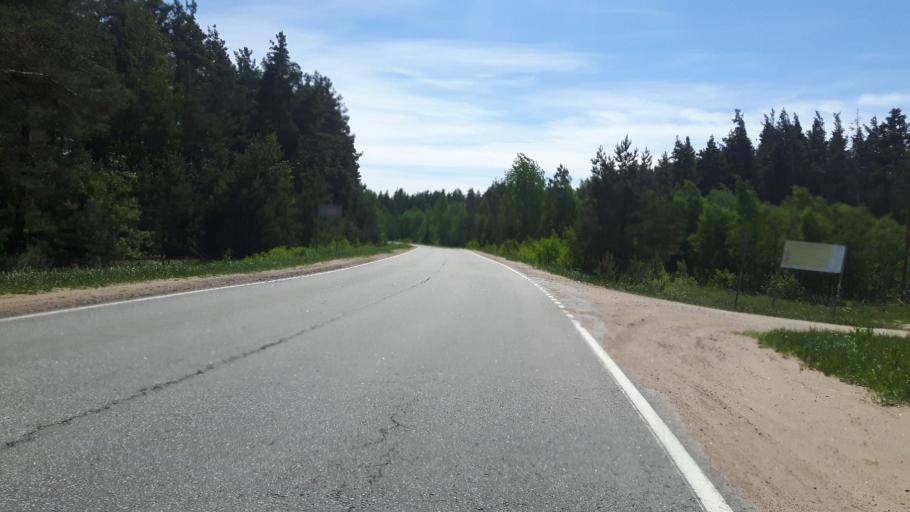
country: EE
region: Ida-Virumaa
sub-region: Narva-Joesuu linn
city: Narva-Joesuu
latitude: 59.5685
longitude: 28.1521
